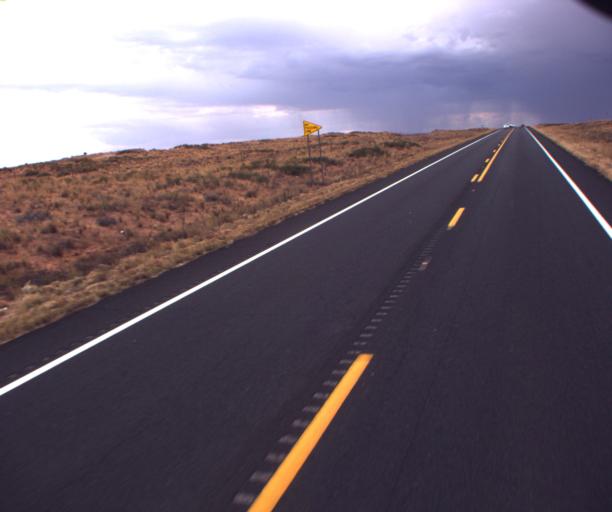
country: US
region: Arizona
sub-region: Coconino County
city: Tuba City
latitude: 36.2980
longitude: -110.9806
